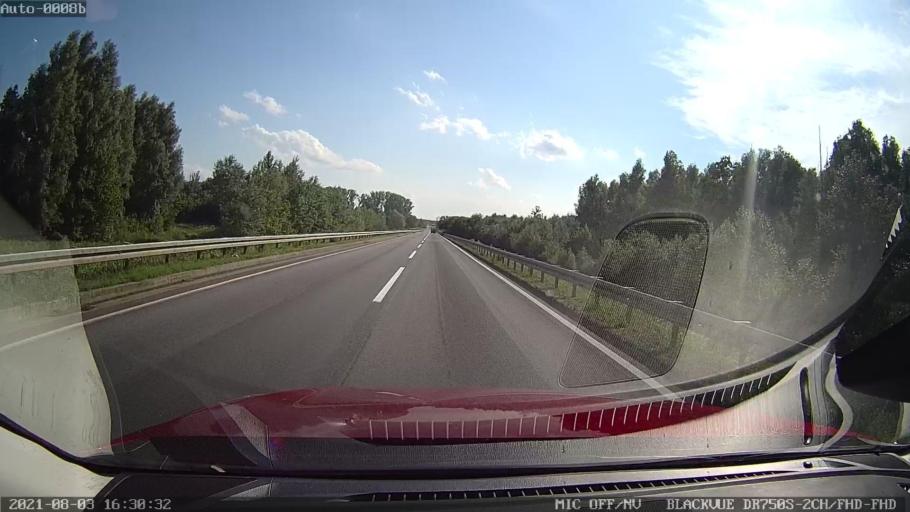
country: HR
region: Osjecko-Baranjska
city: Visnjevac
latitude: 45.5820
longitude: 18.6447
